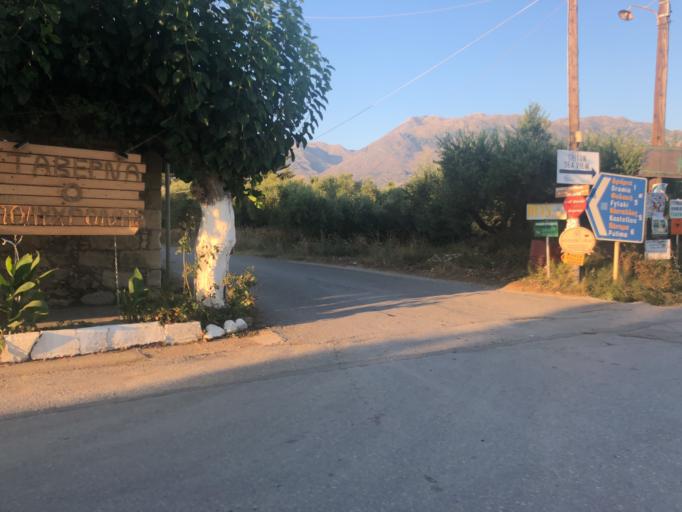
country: GR
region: Crete
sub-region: Nomos Chanias
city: Georgioupolis
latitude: 35.3481
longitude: 24.3017
